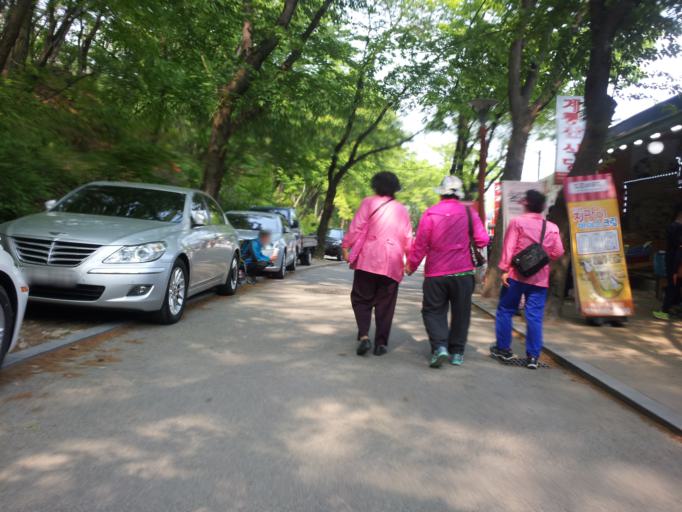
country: KR
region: Chungcheongnam-do
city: Gongju
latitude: 36.3571
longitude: 127.2349
